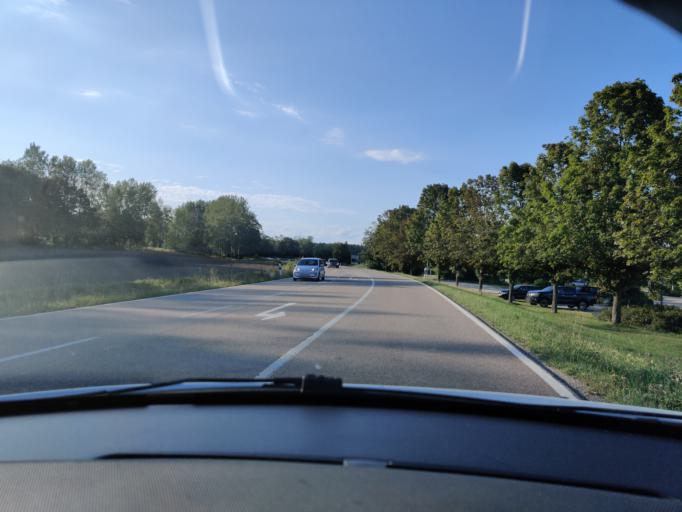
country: DE
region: Bavaria
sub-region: Upper Palatinate
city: Schwarzenfeld
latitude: 49.3990
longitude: 12.1343
